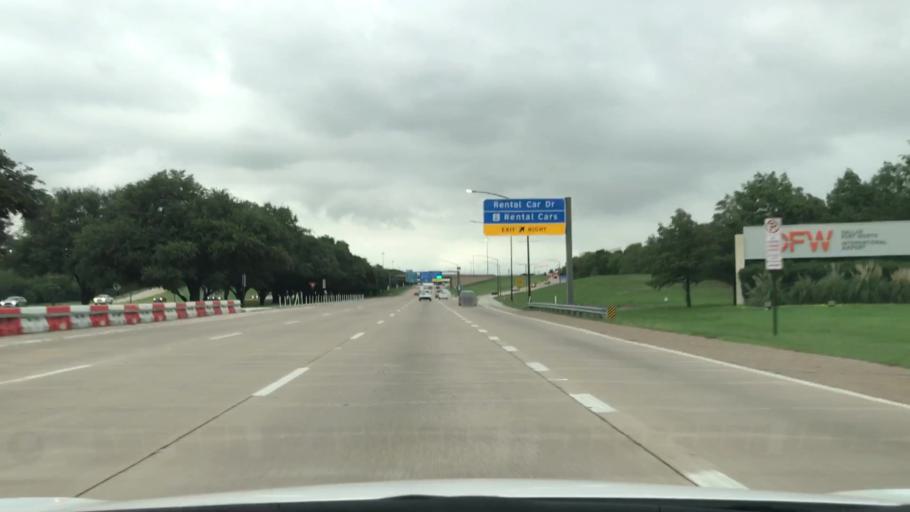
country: US
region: Texas
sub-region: Tarrant County
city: Euless
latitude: 32.8484
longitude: -97.0404
